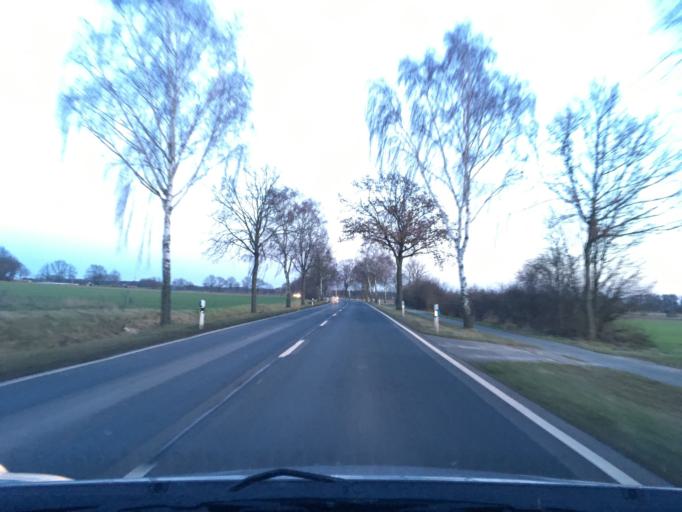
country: DE
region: Lower Saxony
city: Luechow
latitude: 52.9781
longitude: 11.1167
